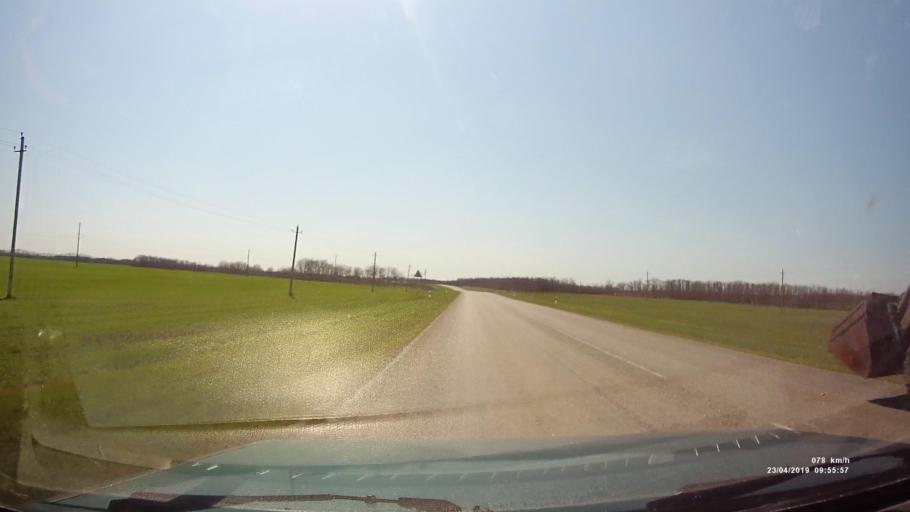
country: RU
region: Rostov
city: Orlovskiy
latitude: 46.8032
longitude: 42.0667
